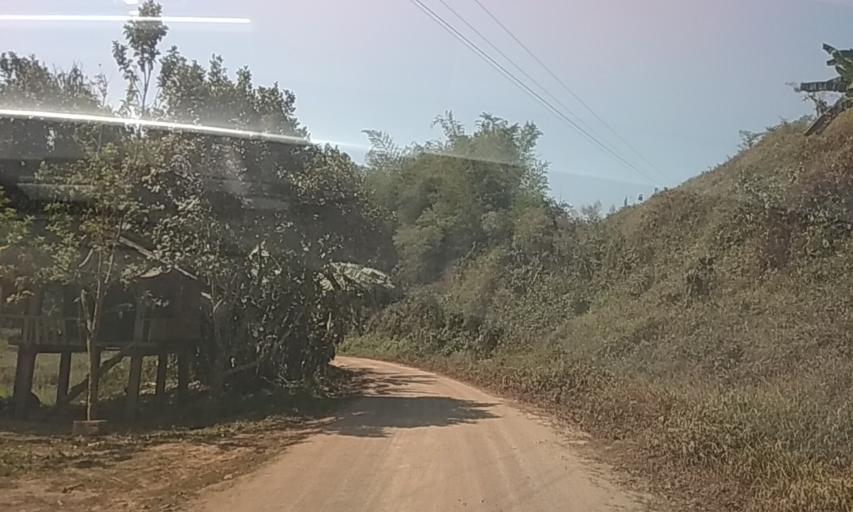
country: CN
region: Yunnan
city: Mengla
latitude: 21.5265
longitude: 101.8358
